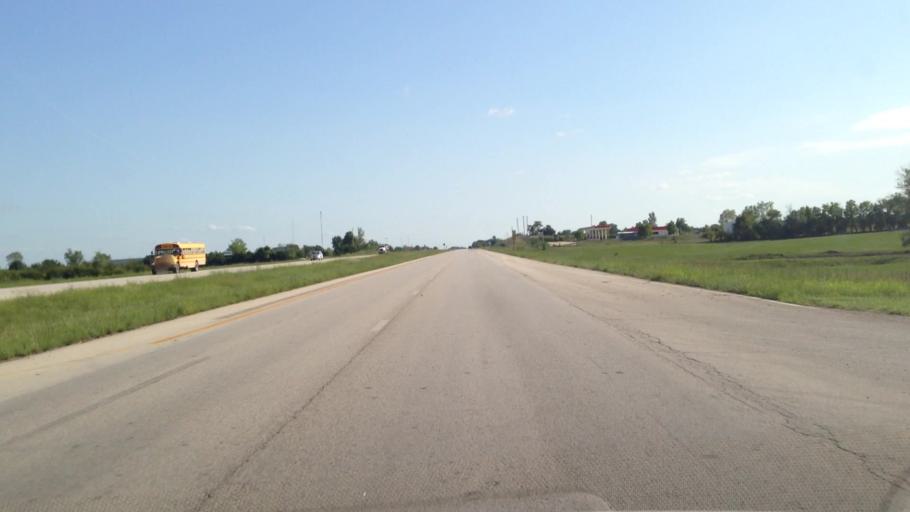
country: US
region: Kansas
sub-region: Bourbon County
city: Fort Scott
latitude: 37.8015
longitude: -94.7052
